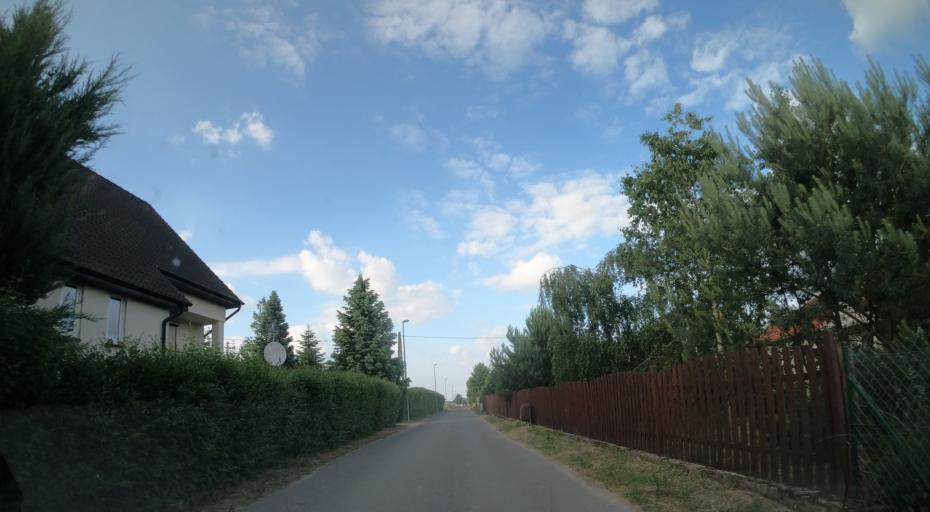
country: PL
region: Lubusz
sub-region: Powiat gorzowski
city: Santok
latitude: 52.7431
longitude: 15.3960
